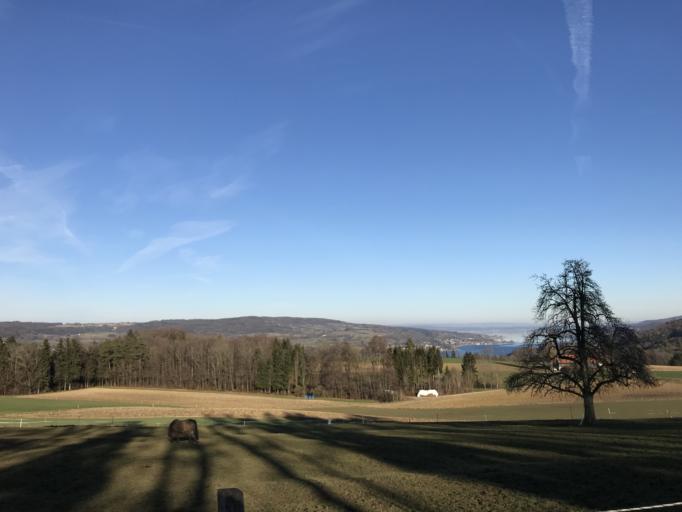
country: CH
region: Thurgau
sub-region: Frauenfeld District
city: Eschenz
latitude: 47.6320
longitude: 8.8580
